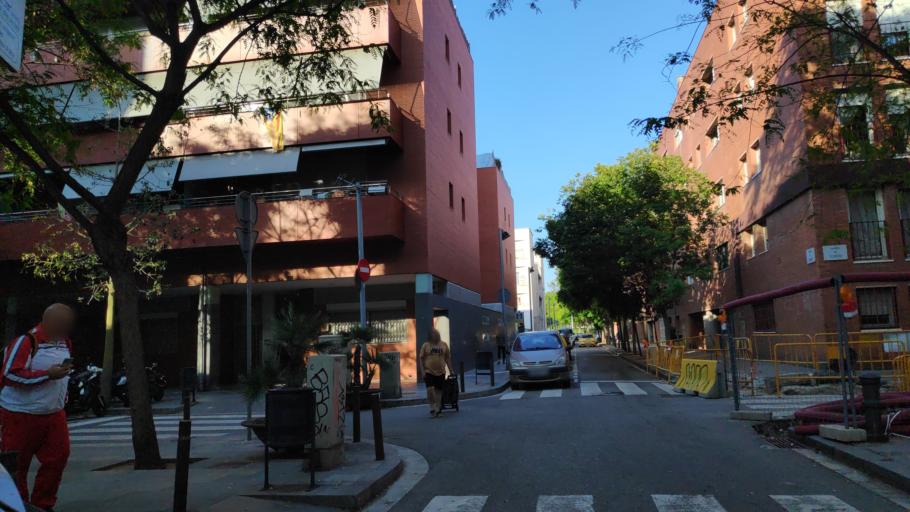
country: ES
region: Catalonia
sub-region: Provincia de Barcelona
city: Ciutat Vella
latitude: 41.3820
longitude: 2.1900
